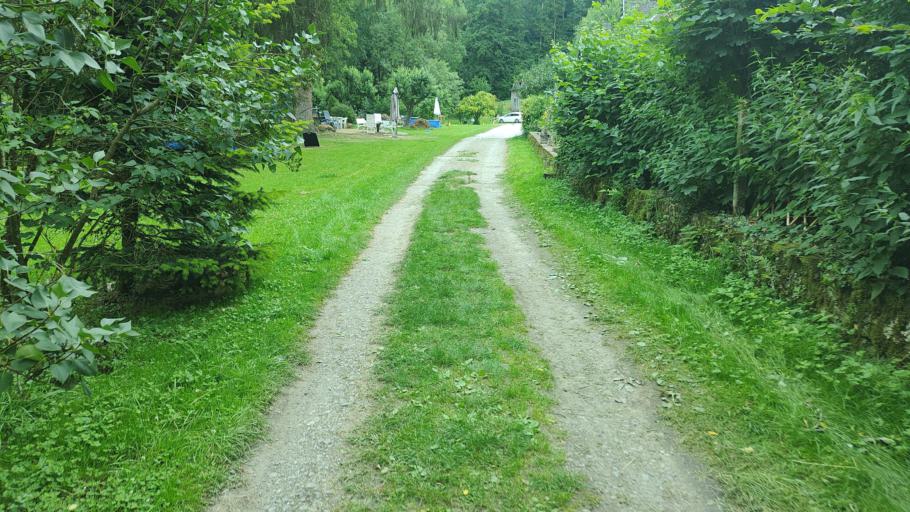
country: BE
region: Wallonia
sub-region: Province du Hainaut
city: Chimay
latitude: 50.0623
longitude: 4.3733
